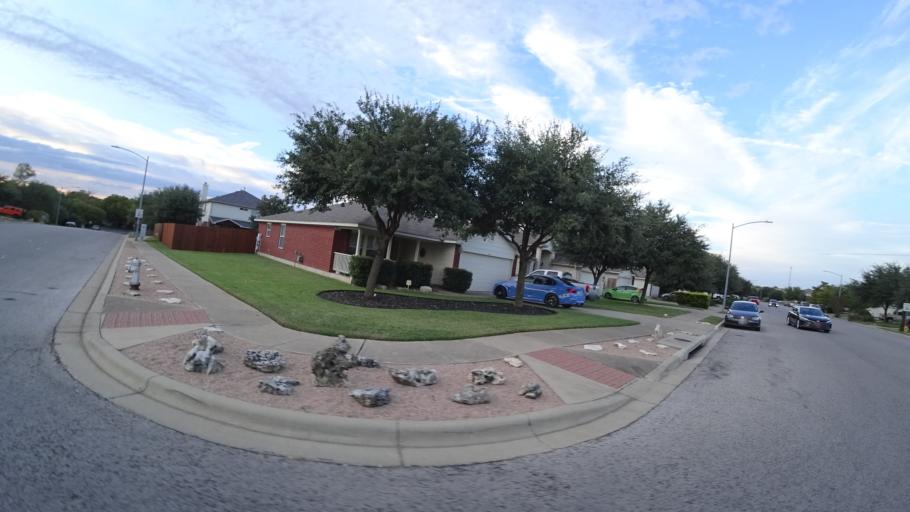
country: US
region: Texas
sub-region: Travis County
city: Austin
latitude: 30.2092
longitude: -97.7622
